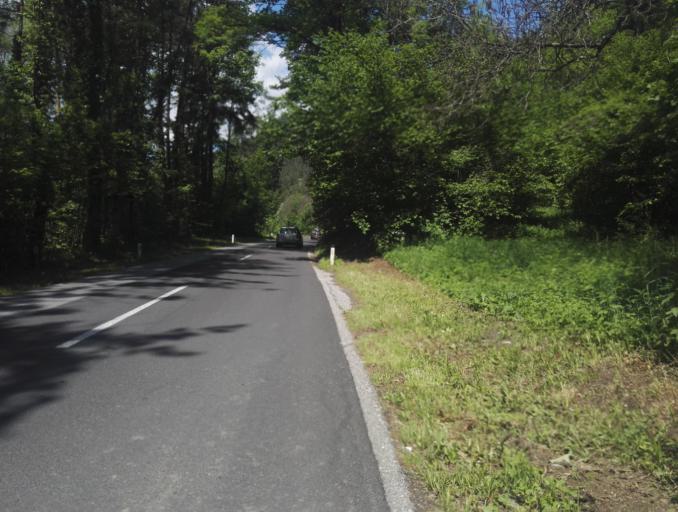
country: AT
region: Styria
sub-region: Politischer Bezirk Graz-Umgebung
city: Deutschfeistritz
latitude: 47.2182
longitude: 15.3079
